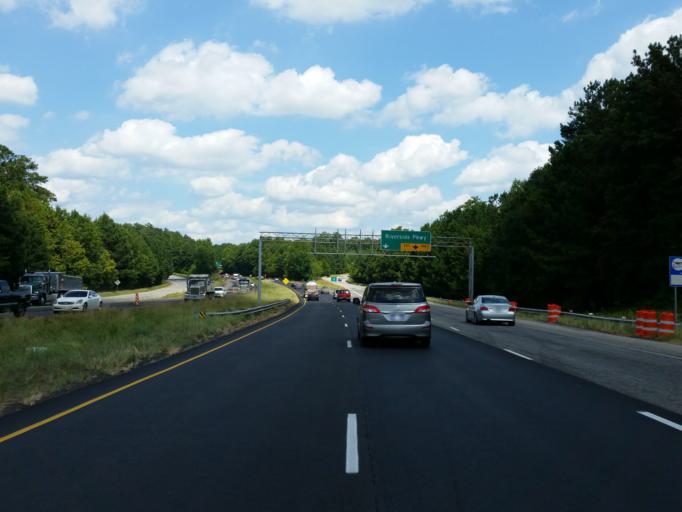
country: US
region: Georgia
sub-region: Gwinnett County
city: Lawrenceville
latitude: 33.9587
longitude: -84.0423
